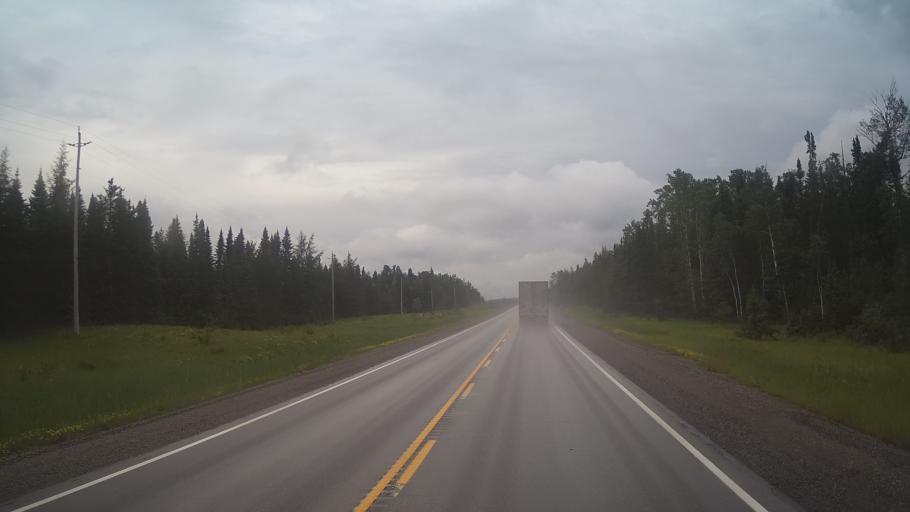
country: CA
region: Ontario
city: Neebing
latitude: 48.6344
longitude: -89.8949
